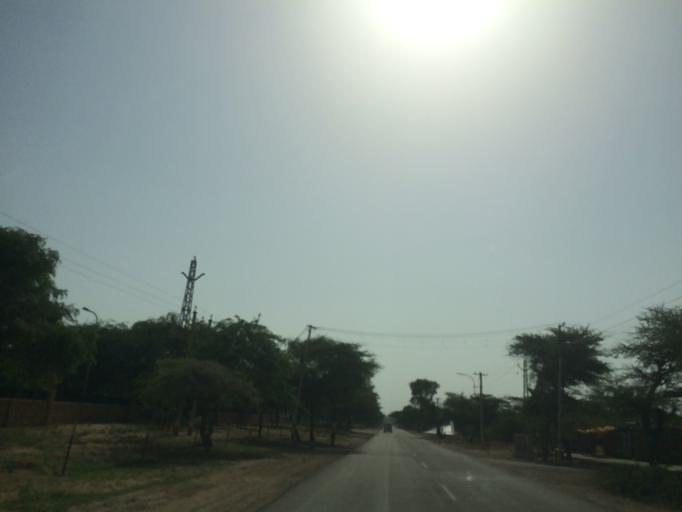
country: IN
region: Rajasthan
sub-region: Jaisalmer
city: Jaisalmer
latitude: 26.9158
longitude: 70.8919
